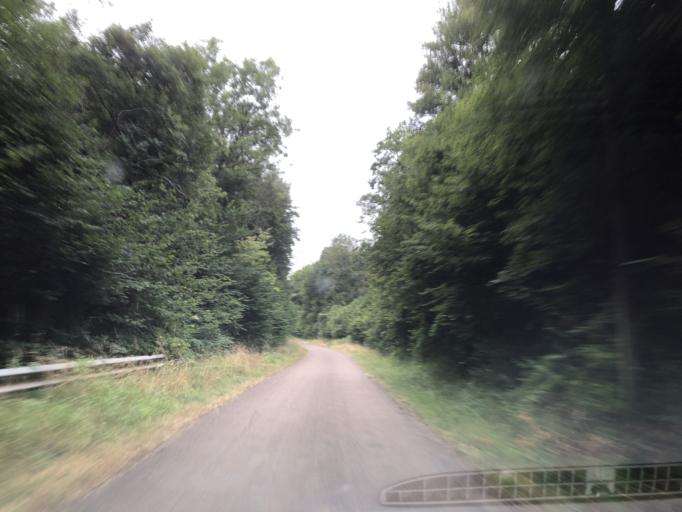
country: FR
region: Bourgogne
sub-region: Departement de l'Yonne
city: Aillant-sur-Tholon
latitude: 47.9184
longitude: 3.3205
